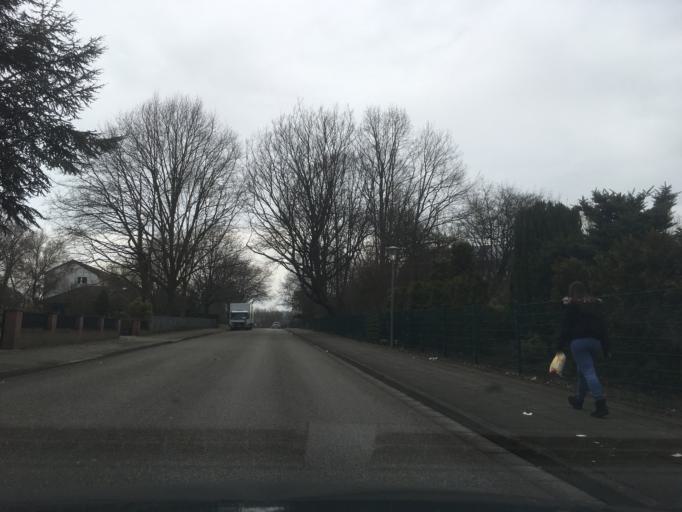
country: DE
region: North Rhine-Westphalia
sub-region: Regierungsbezirk Munster
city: Gladbeck
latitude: 51.5690
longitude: 7.0100
